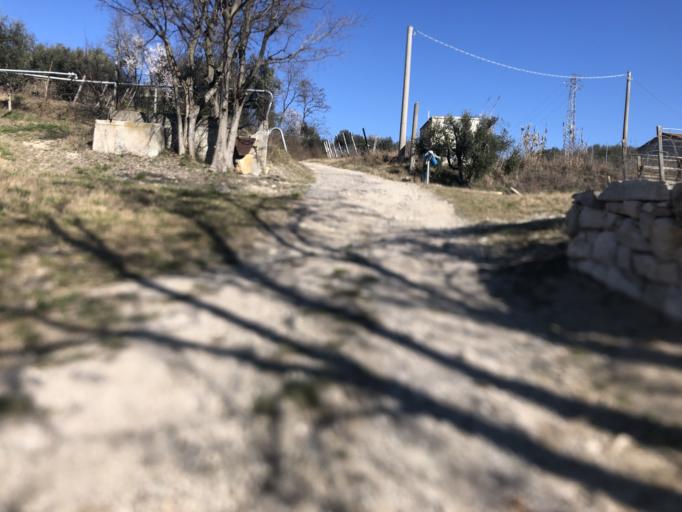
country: IT
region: Veneto
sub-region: Provincia di Verona
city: San Giorgio in Salici
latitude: 45.4352
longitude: 10.8128
